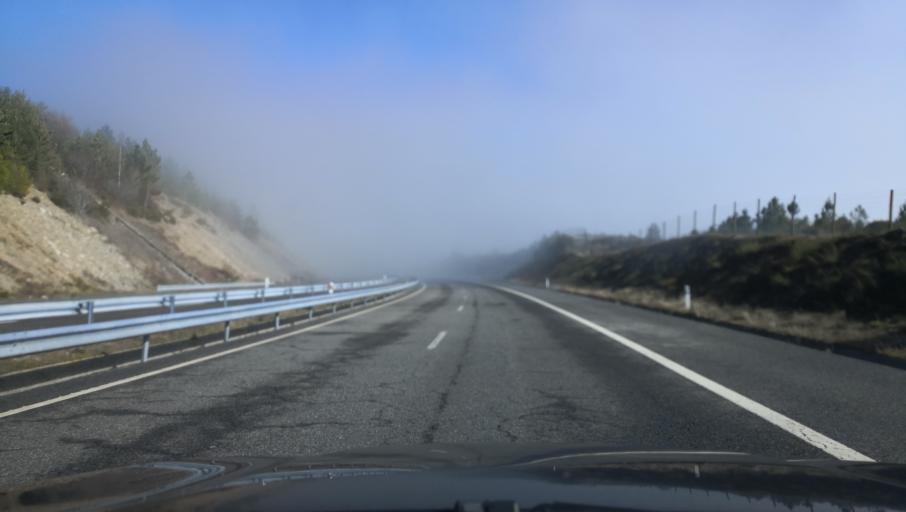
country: PT
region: Vila Real
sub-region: Vila Pouca de Aguiar
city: Vila Pouca de Aguiar
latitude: 41.5189
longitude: -7.6478
